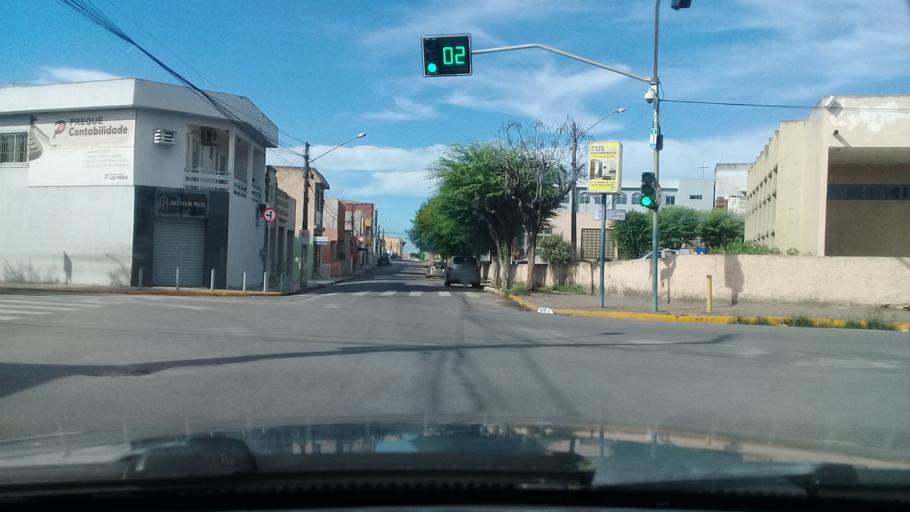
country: BR
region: Pernambuco
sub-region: Vitoria De Santo Antao
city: Vitoria de Santo Antao
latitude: -8.1146
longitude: -35.2925
